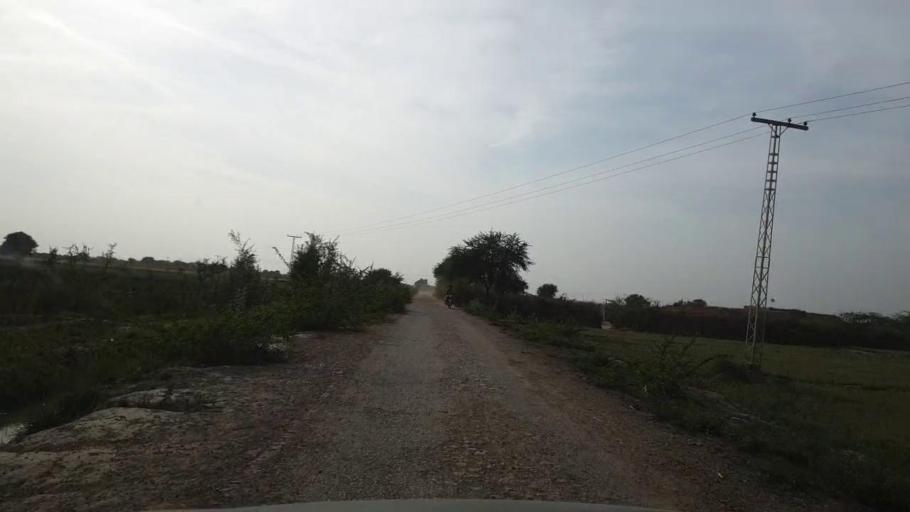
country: PK
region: Sindh
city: Kunri
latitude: 25.1459
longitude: 69.5033
